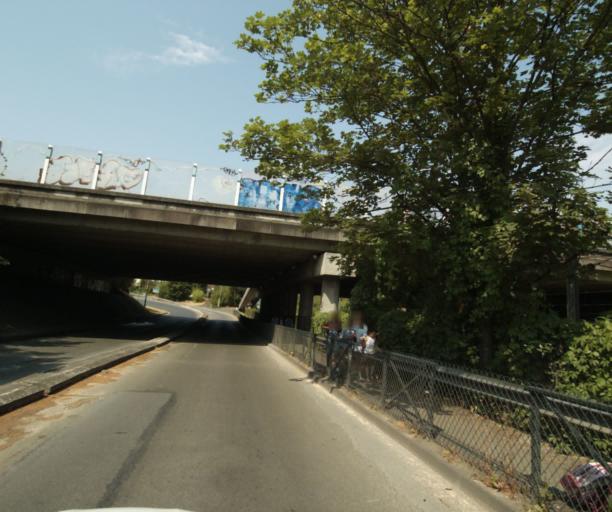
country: FR
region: Ile-de-France
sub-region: Departement des Yvelines
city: Conflans-Sainte-Honorine
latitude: 48.9921
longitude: 2.0815
